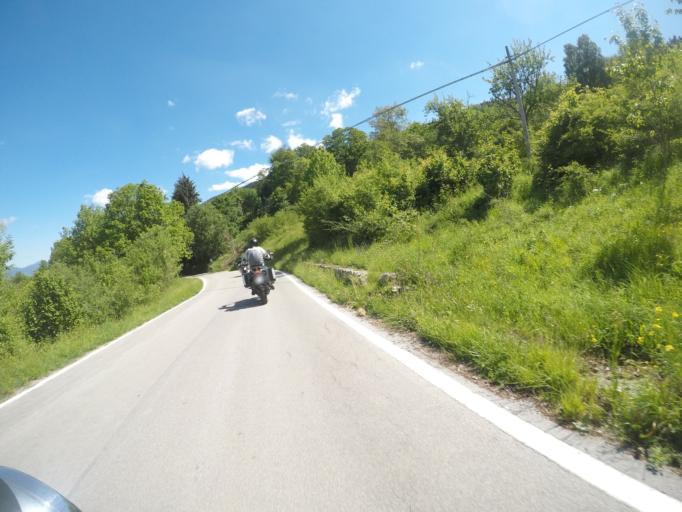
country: IT
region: Tuscany
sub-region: Provincia di Lucca
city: Careggine
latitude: 44.1071
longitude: 10.3330
